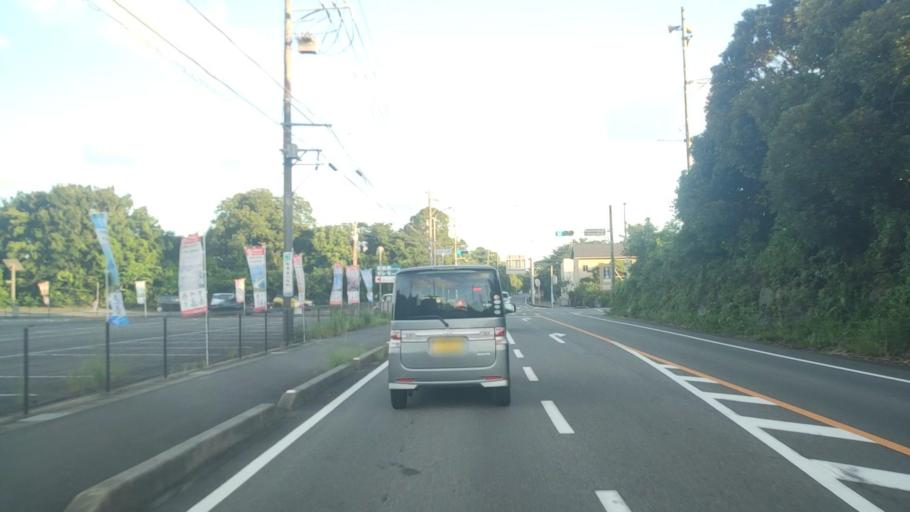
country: JP
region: Mie
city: Toba
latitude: 34.3214
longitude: 136.8286
